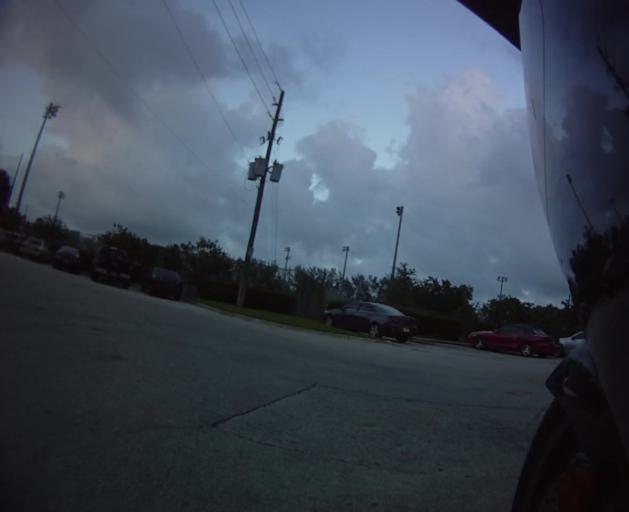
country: US
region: Florida
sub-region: Miami-Dade County
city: Miami Beach
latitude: 25.7853
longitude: -80.1387
